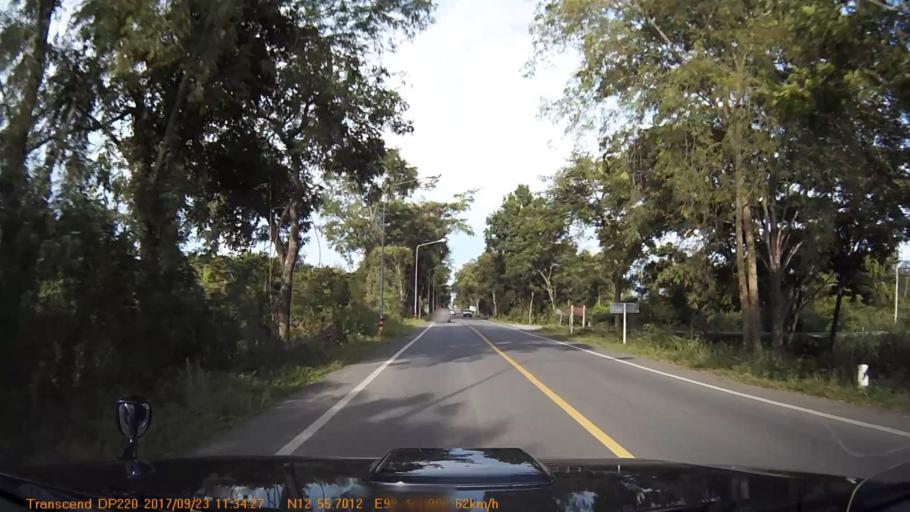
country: TH
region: Phetchaburi
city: Kaeng Krachan
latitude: 12.9283
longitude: 99.7348
